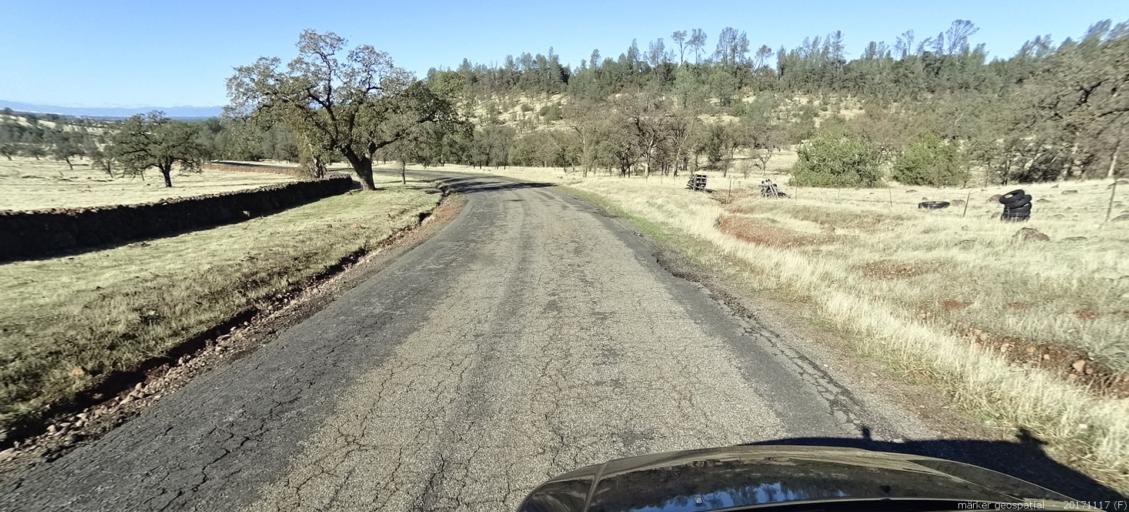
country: US
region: California
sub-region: Shasta County
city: Cottonwood
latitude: 40.4398
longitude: -122.1246
